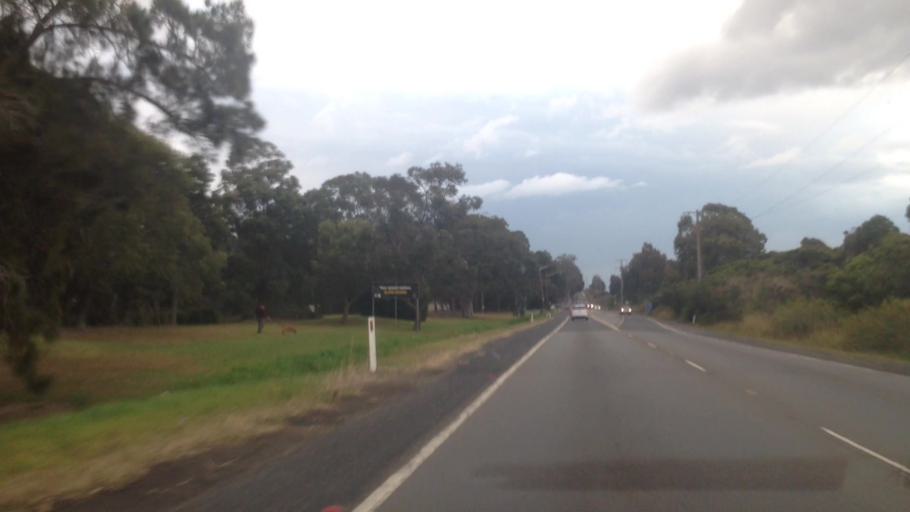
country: AU
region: New South Wales
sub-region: Wyong Shire
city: Chittaway Bay
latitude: -33.2781
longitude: 151.4278
